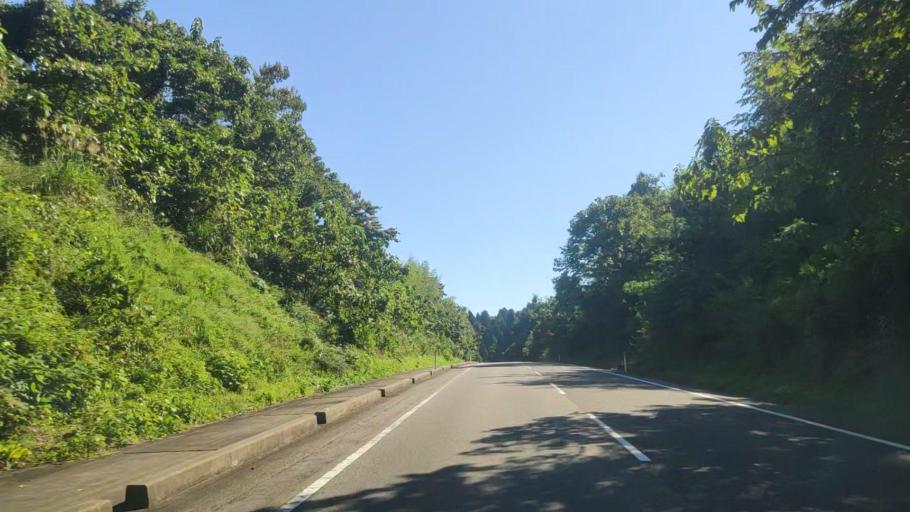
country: JP
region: Ishikawa
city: Nanao
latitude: 37.3800
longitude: 137.2338
